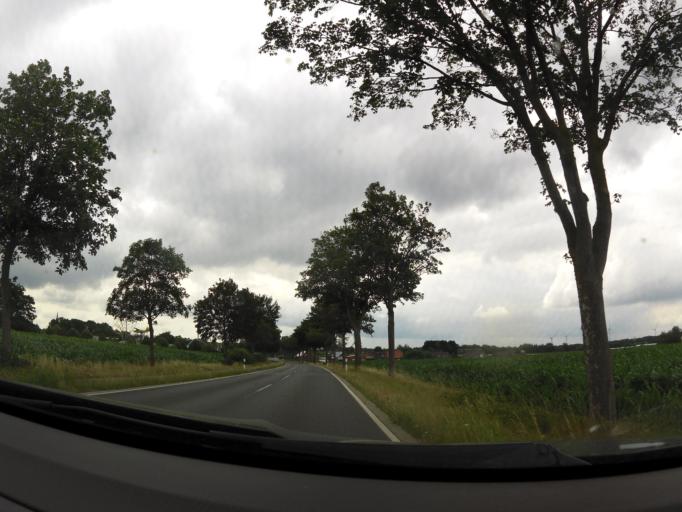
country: DE
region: North Rhine-Westphalia
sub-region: Regierungsbezirk Dusseldorf
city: Kevelaer
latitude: 51.5599
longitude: 6.2131
